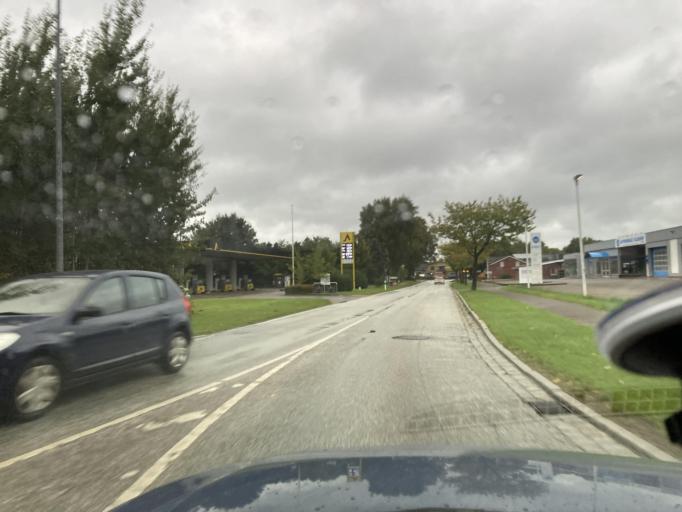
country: DE
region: Schleswig-Holstein
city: Elsdorf-Westermuhlen
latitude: 54.2546
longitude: 9.5334
